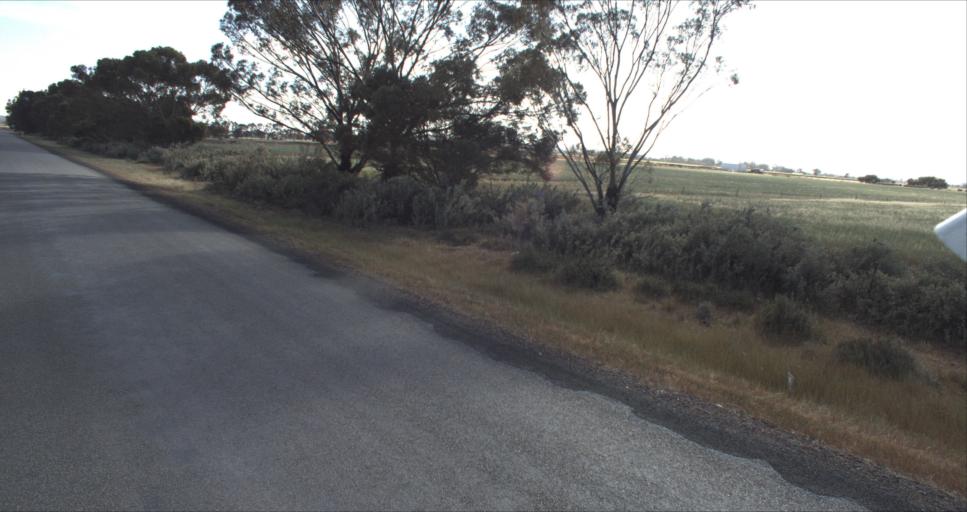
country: AU
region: New South Wales
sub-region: Leeton
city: Leeton
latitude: -34.5059
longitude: 146.3931
